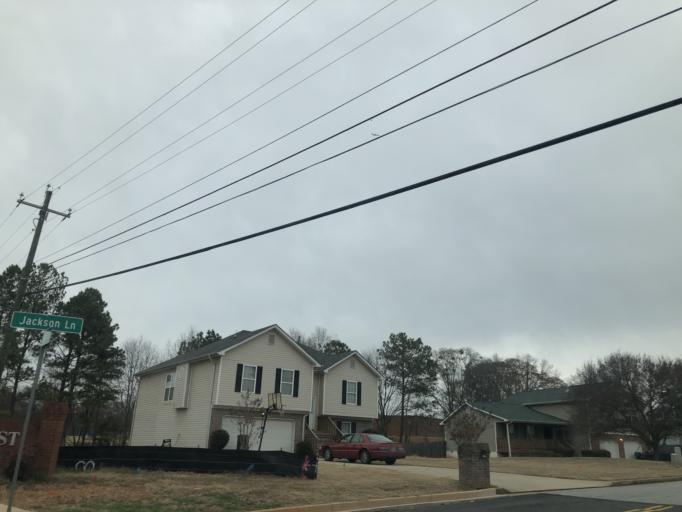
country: US
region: Georgia
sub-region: Clayton County
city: Conley
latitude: 33.6144
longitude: -84.2714
